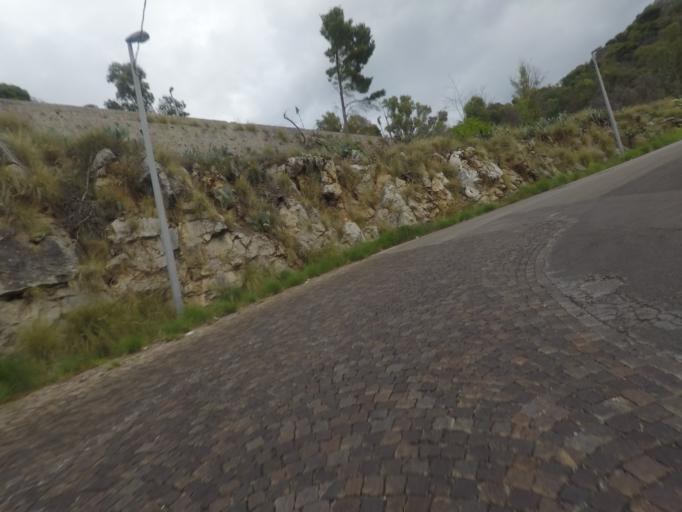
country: IT
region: Sicily
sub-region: Palermo
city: Palermo
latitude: 38.1543
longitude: 13.3603
